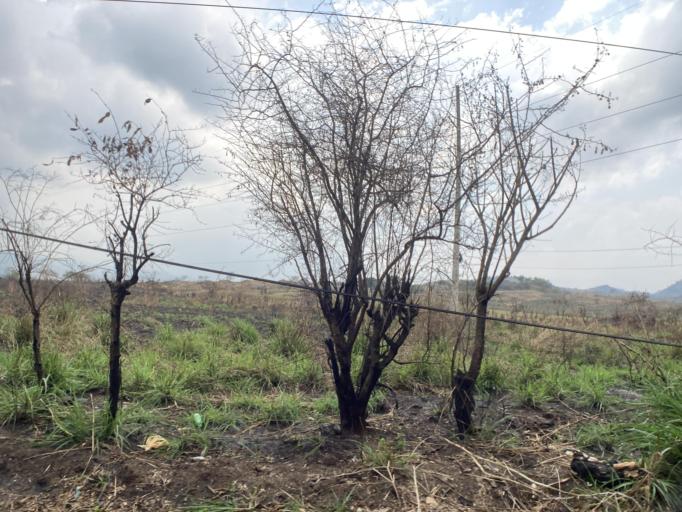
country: GT
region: Guatemala
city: Fraijanes
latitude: 14.3803
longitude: -90.4894
